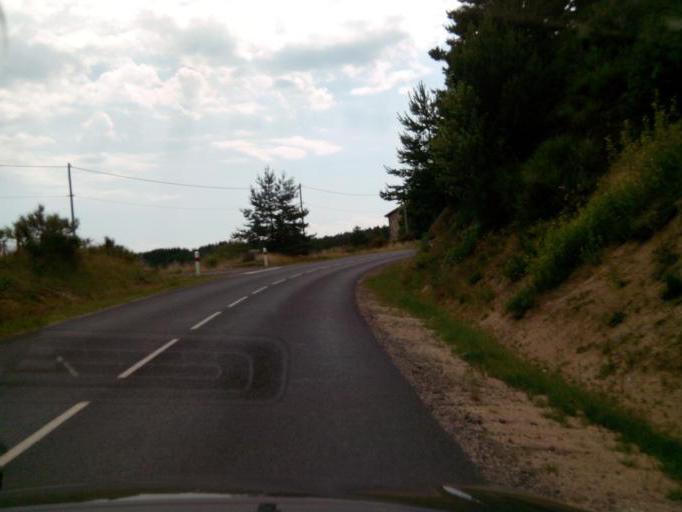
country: FR
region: Rhone-Alpes
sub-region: Departement de la Loire
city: Saint-Bonnet-le-Chateau
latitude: 45.3890
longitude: 4.0134
